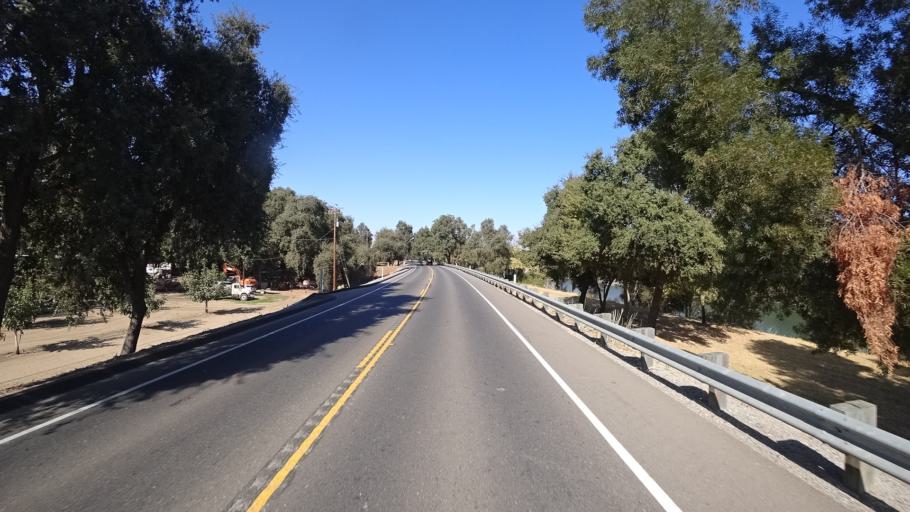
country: US
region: California
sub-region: Yolo County
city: West Sacramento
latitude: 38.6407
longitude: -121.5656
